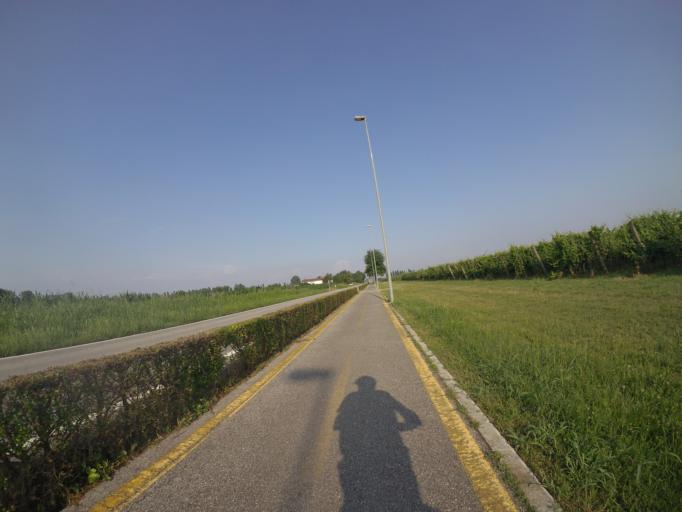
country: IT
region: Friuli Venezia Giulia
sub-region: Provincia di Udine
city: Codroipo
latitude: 45.9576
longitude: 13.0016
